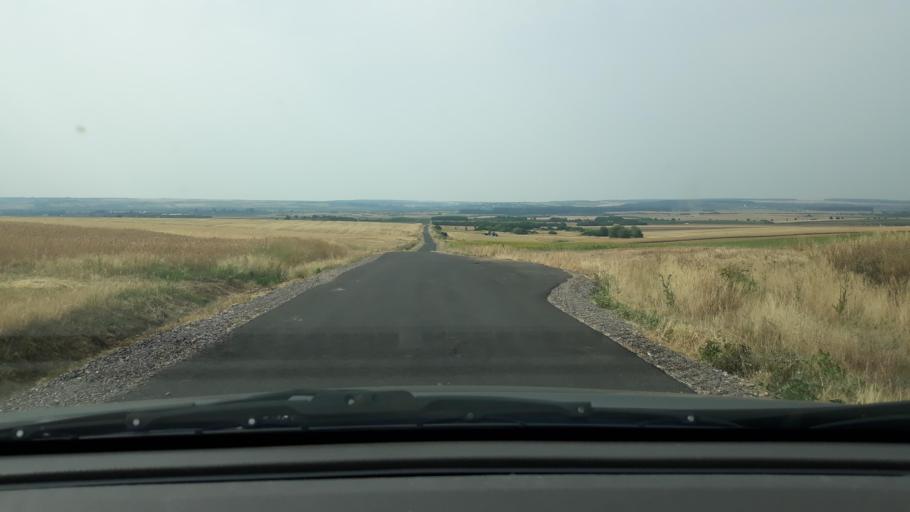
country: RO
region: Bihor
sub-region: Comuna Chislaz
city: Misca
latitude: 47.2694
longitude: 22.2861
